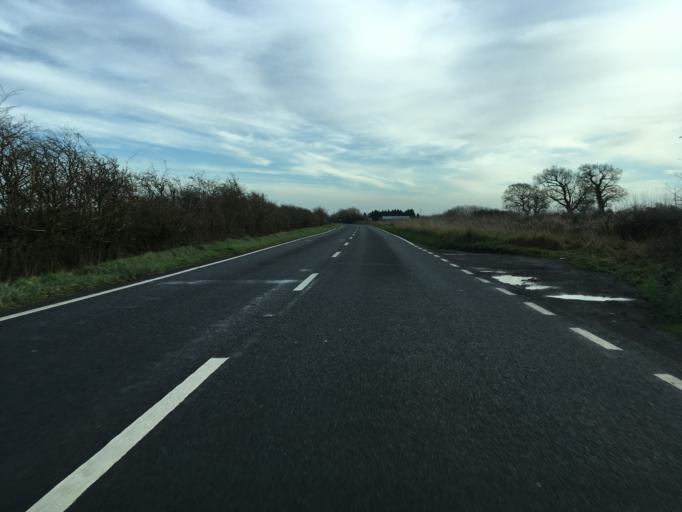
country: GB
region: England
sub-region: South Gloucestershire
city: Alveston
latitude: 51.5697
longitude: -2.5151
